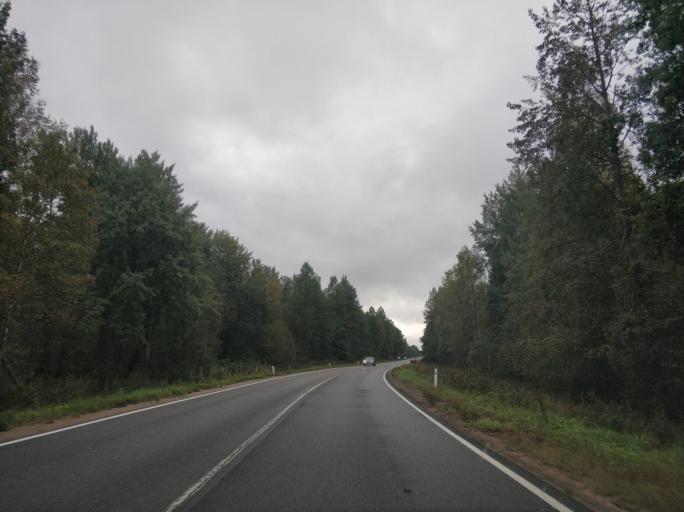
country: RU
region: Leningrad
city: Borisova Griva
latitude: 60.1321
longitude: 30.9629
